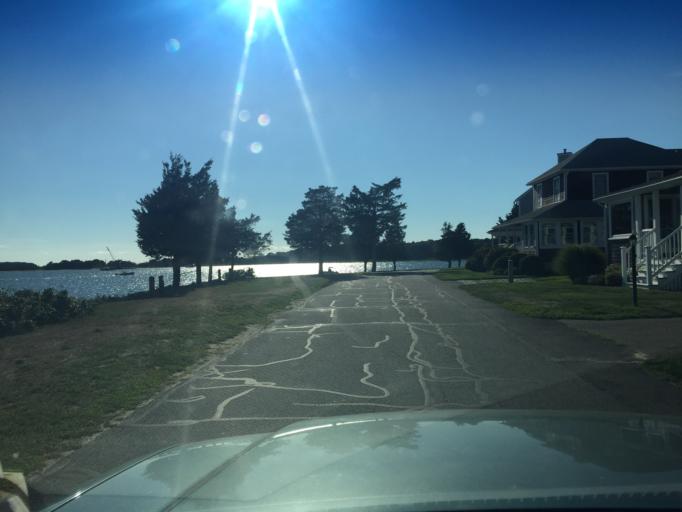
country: US
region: Massachusetts
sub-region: Barnstable County
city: Pocasset
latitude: 41.6817
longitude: -70.6261
